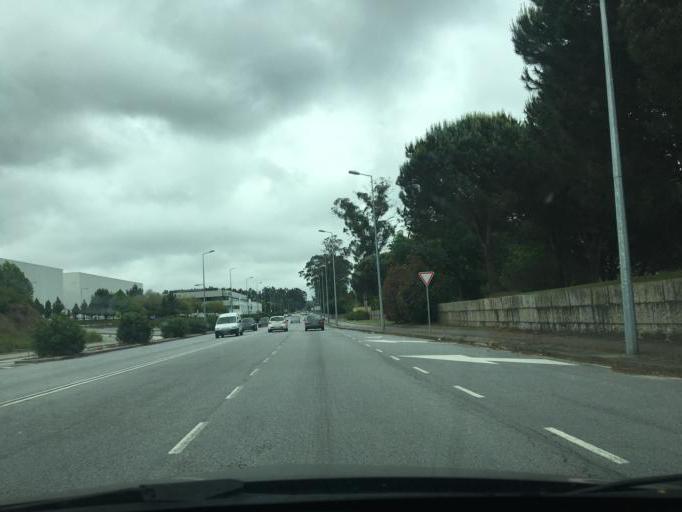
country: PT
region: Porto
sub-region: Maia
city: Maia
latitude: 41.2380
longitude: -8.6433
